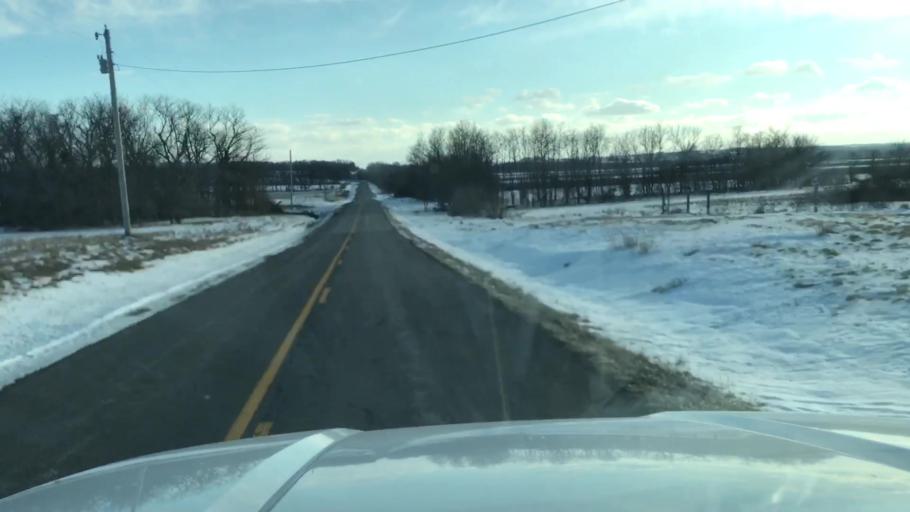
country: US
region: Missouri
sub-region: Holt County
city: Oregon
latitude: 40.1110
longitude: -95.0226
